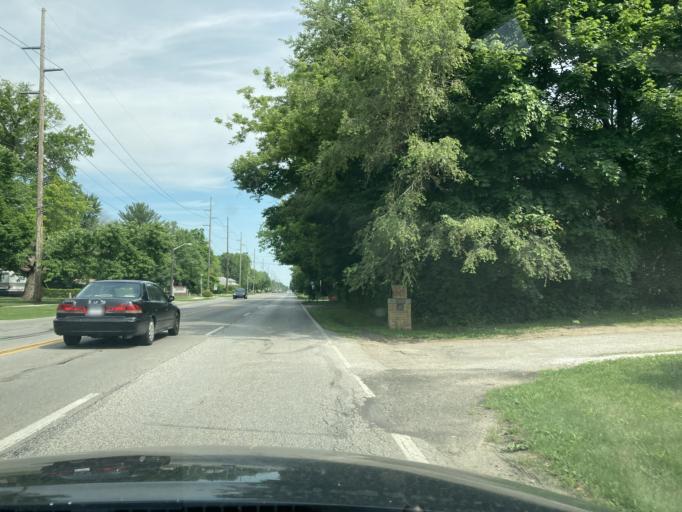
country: US
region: Indiana
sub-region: Marion County
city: Broad Ripple
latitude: 39.8453
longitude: -86.1906
